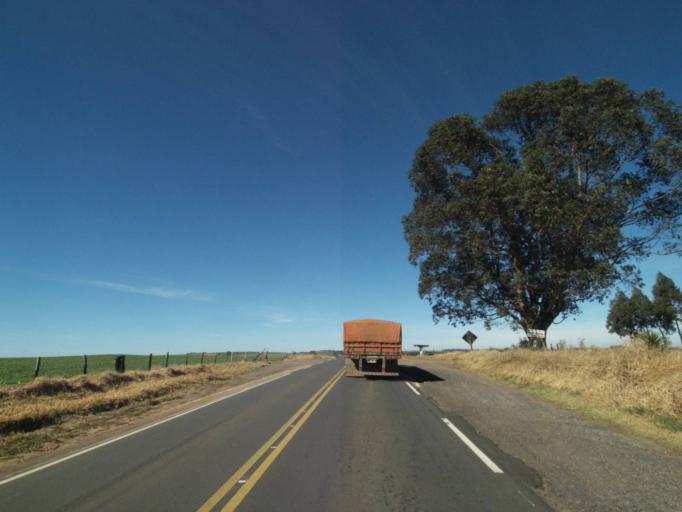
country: BR
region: Parana
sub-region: Tibagi
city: Tibagi
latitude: -24.6245
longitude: -50.2486
